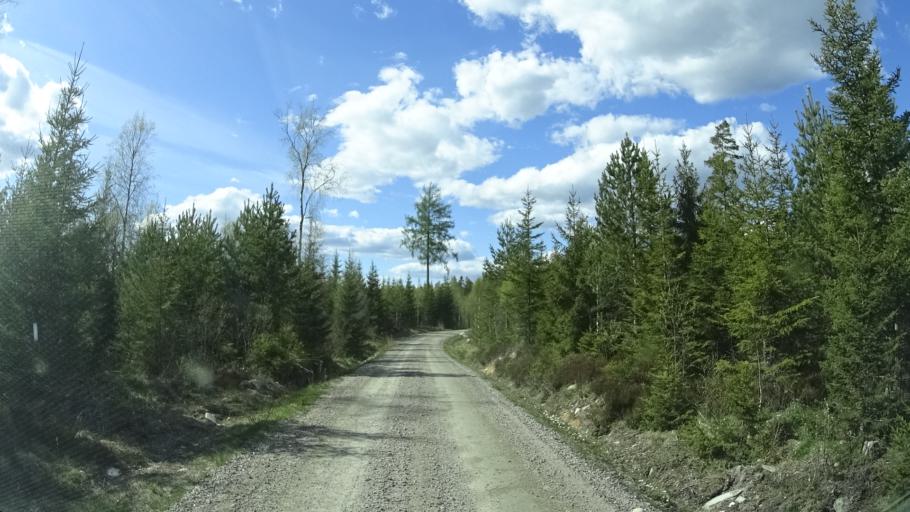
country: SE
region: OErebro
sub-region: Orebro Kommun
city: Garphyttan
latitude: 59.4205
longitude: 14.8669
